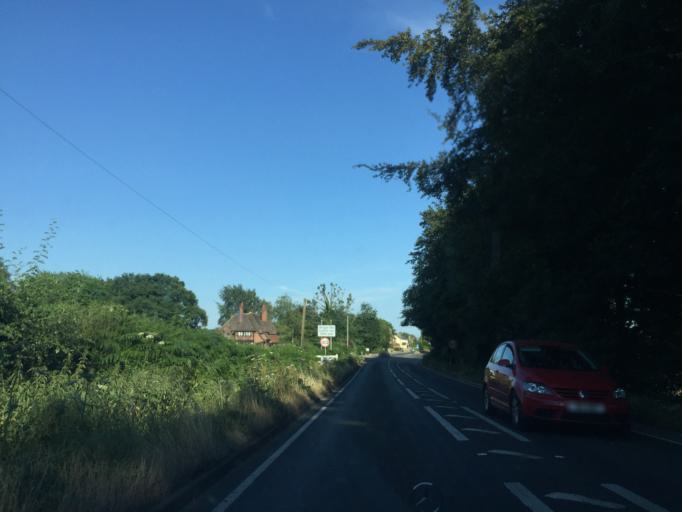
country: GB
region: England
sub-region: Oxfordshire
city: Rotherfield Peppard
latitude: 51.5627
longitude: -0.9576
